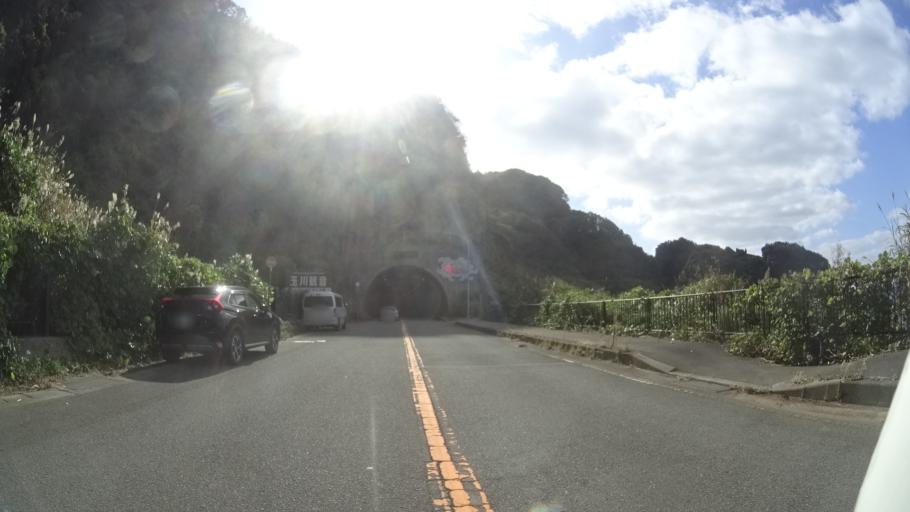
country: JP
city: Asahi
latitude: 35.9785
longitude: 135.9611
